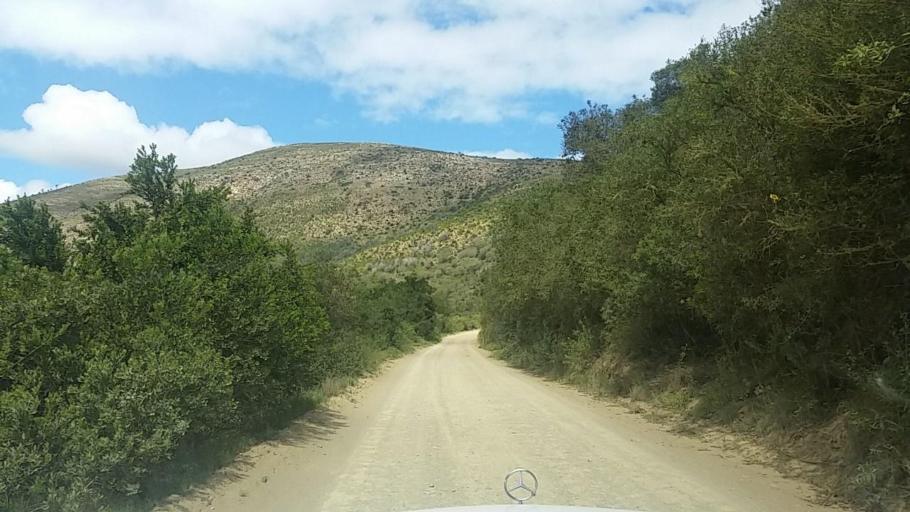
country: ZA
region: Western Cape
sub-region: Eden District Municipality
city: Knysna
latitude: -33.8144
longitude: 23.1749
